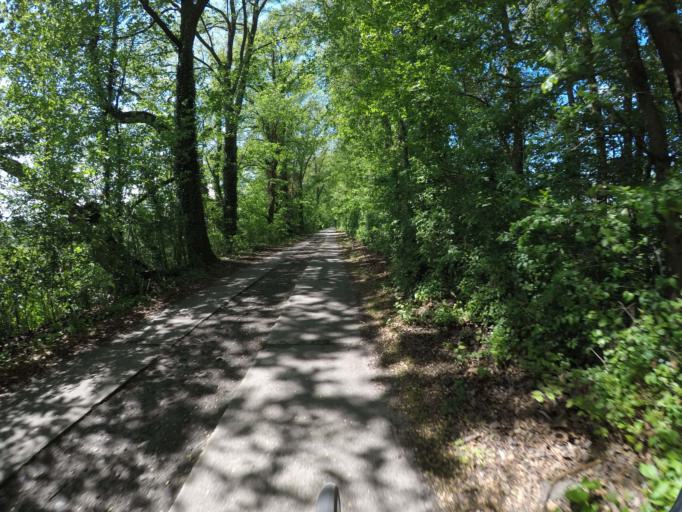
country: DE
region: Brandenburg
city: Werder
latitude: 52.4274
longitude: 12.9457
